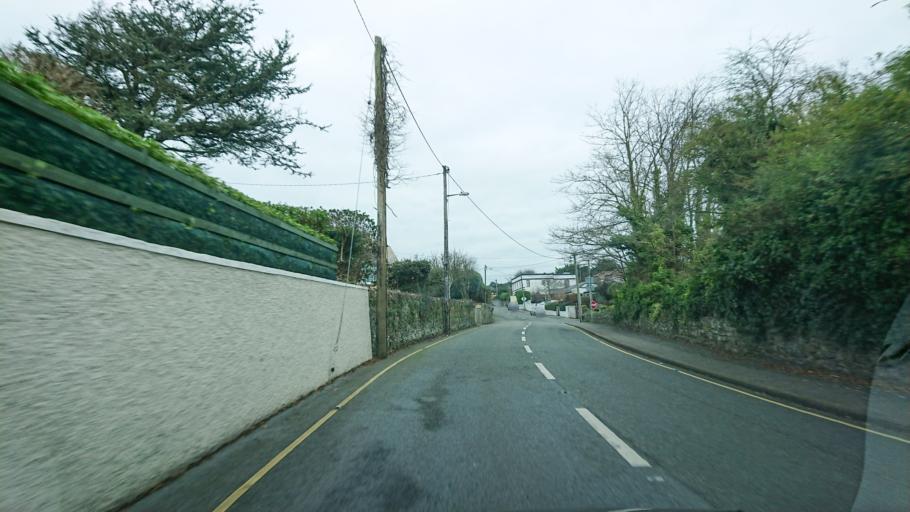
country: IE
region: Munster
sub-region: Waterford
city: Tra Mhor
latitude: 52.1549
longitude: -7.1619
